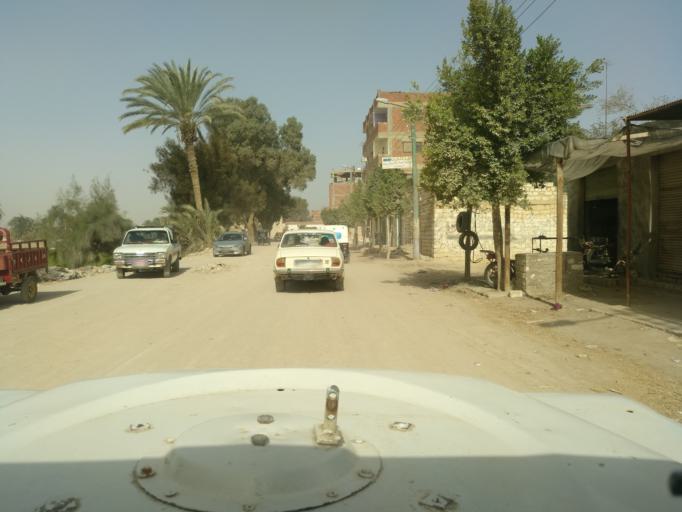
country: EG
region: Al Buhayrah
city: Beheira
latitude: 30.3714
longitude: 30.3543
